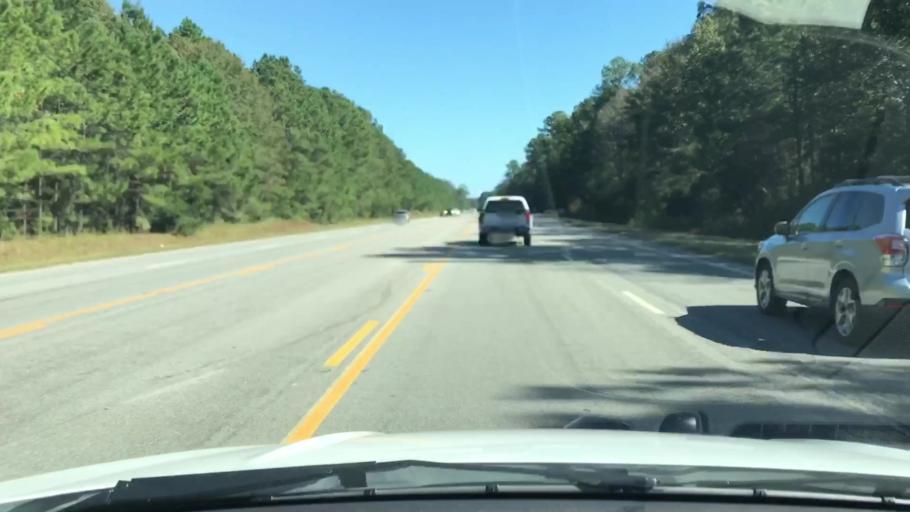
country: US
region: South Carolina
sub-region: Beaufort County
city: Bluffton
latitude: 32.3542
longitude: -80.9068
